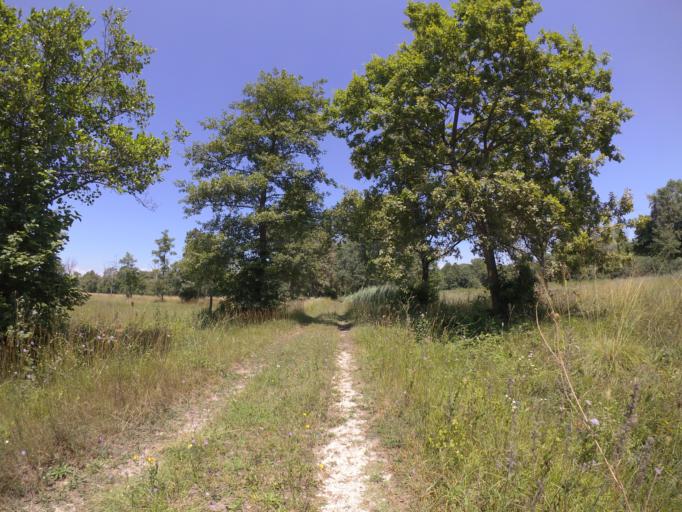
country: IT
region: Friuli Venezia Giulia
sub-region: Provincia di Udine
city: Bertiolo
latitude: 45.9195
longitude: 13.0793
